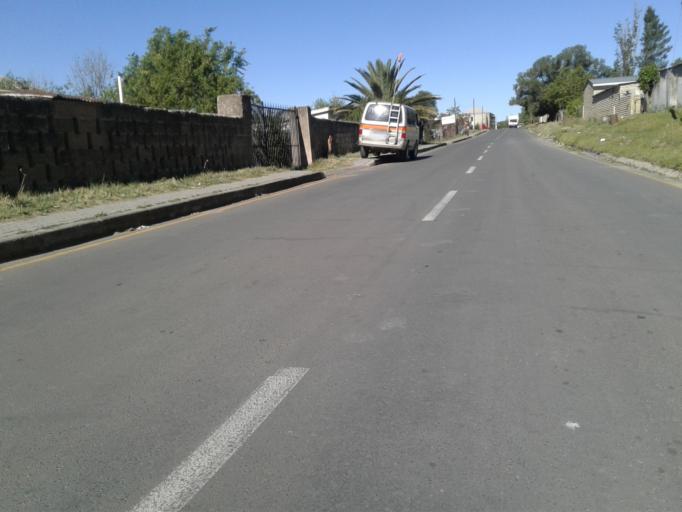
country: LS
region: Maseru
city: Maseru
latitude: -29.3007
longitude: 27.4692
